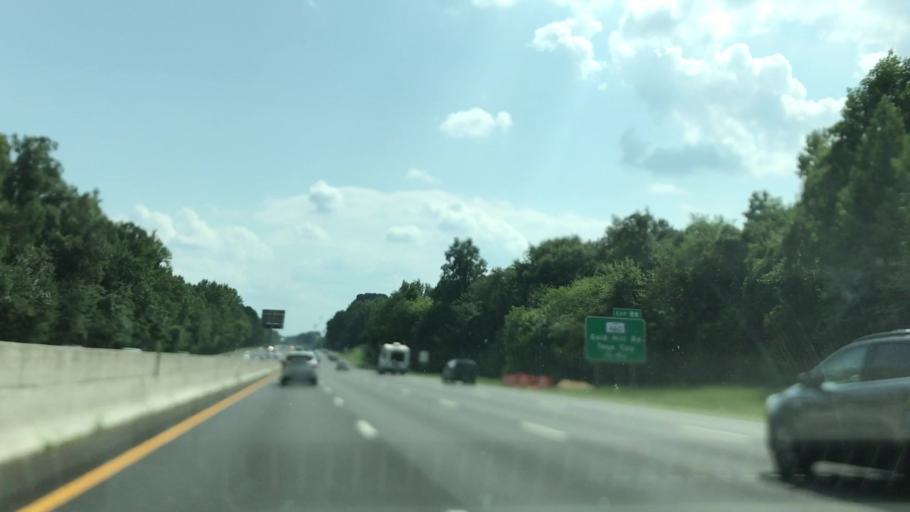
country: US
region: North Carolina
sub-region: Mecklenburg County
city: Pineville
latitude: 35.0730
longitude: -80.9476
